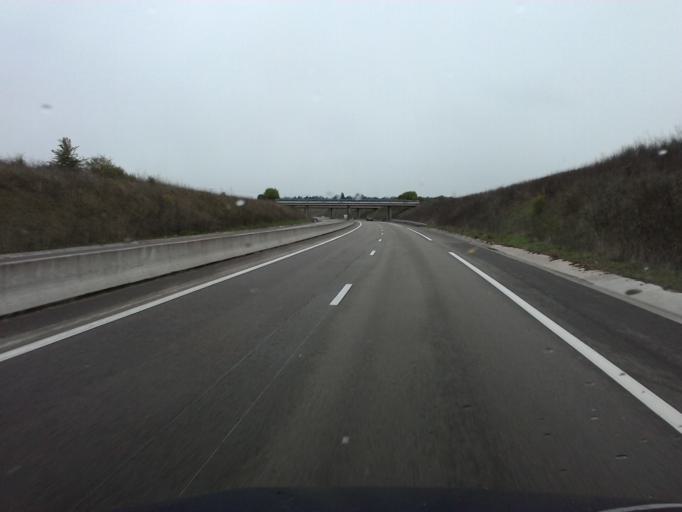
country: FR
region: Champagne-Ardenne
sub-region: Departement de la Haute-Marne
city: Chaumont
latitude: 48.1304
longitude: 5.1076
